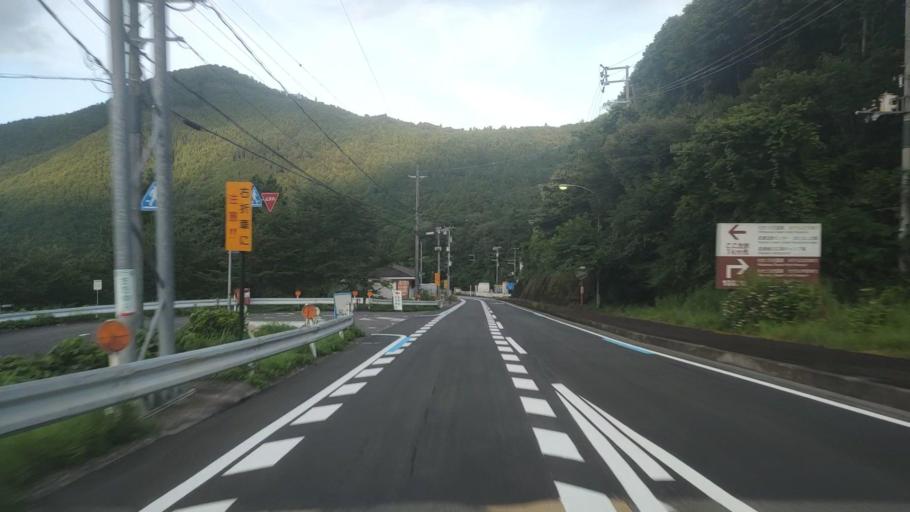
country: JP
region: Wakayama
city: Shingu
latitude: 33.8181
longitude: 135.7620
